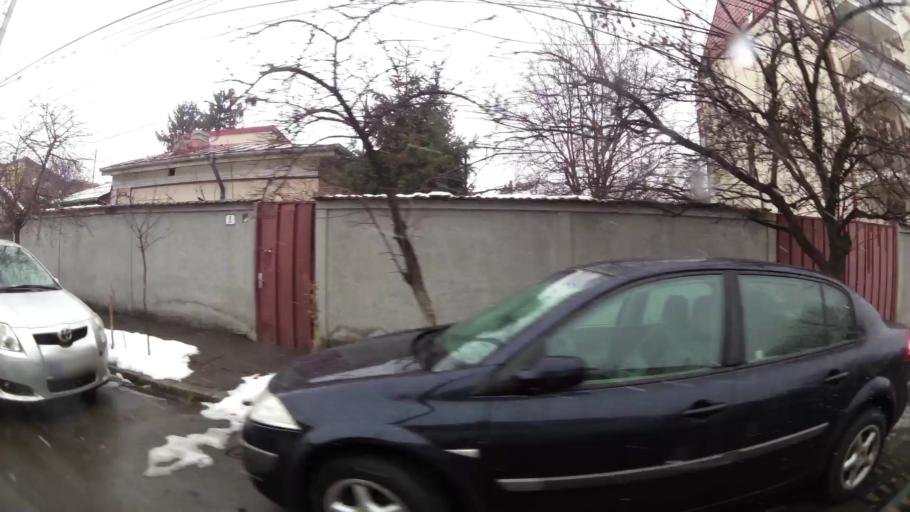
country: RO
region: Ilfov
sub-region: Comuna Chiajna
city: Rosu
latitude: 44.4923
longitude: 26.0430
